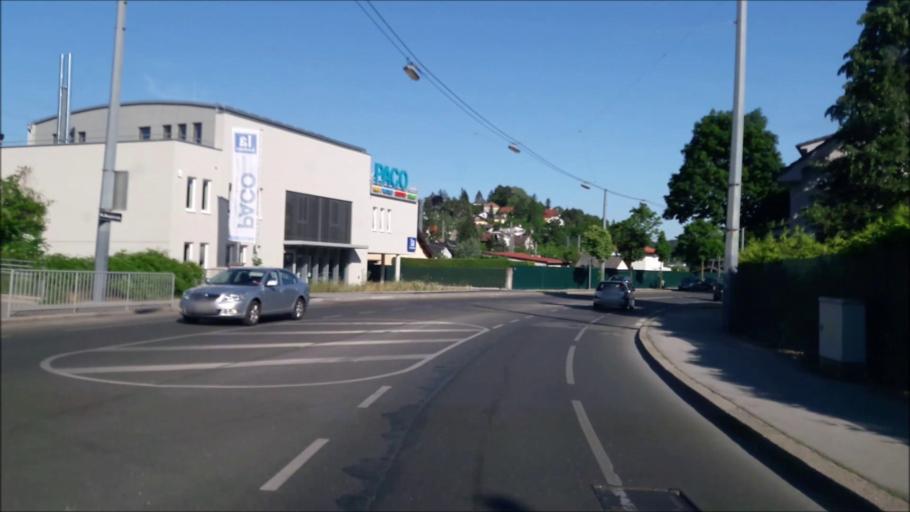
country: AT
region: Lower Austria
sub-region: Politischer Bezirk Wien-Umgebung
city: Purkersdorf
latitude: 48.2076
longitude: 16.2321
